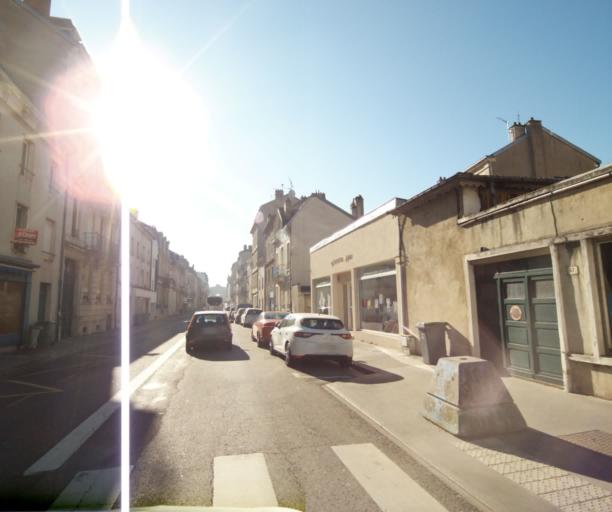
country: FR
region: Lorraine
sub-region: Departement de Meurthe-et-Moselle
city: Nancy
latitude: 48.6978
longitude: 6.1853
